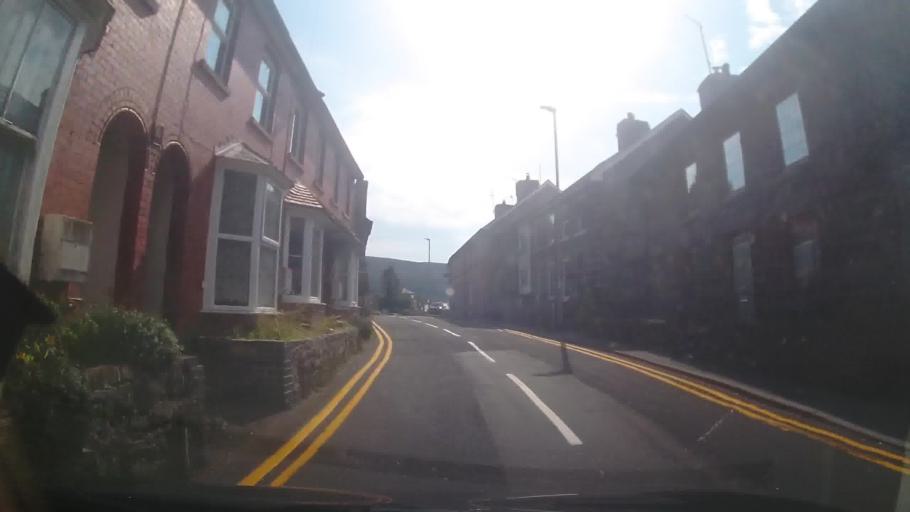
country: GB
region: Wales
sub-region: Sir Powys
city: Rhayader
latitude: 52.3027
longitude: -3.5129
